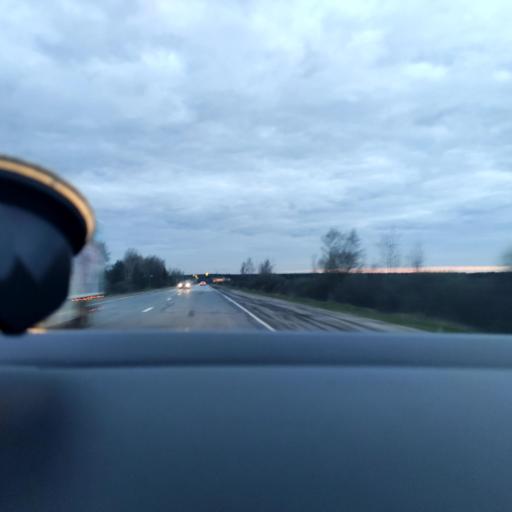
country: RU
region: Moskovskaya
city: Yegor'yevsk
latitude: 55.4362
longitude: 39.0241
